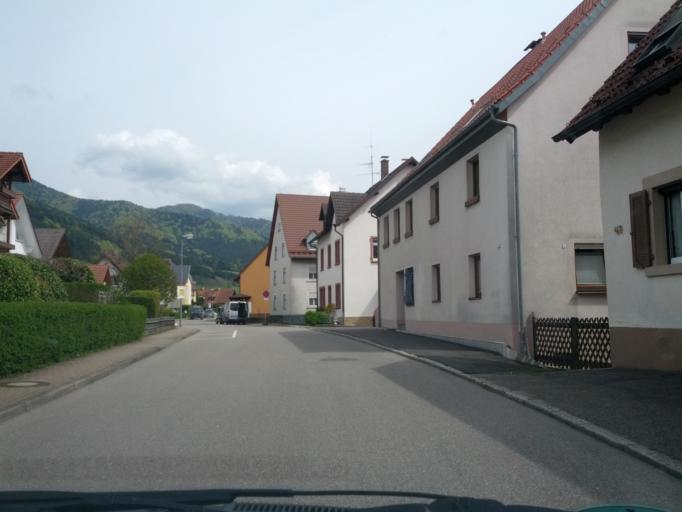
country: DE
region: Baden-Wuerttemberg
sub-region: Freiburg Region
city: Gutach im Breisgau
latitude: 48.1219
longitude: 8.0057
